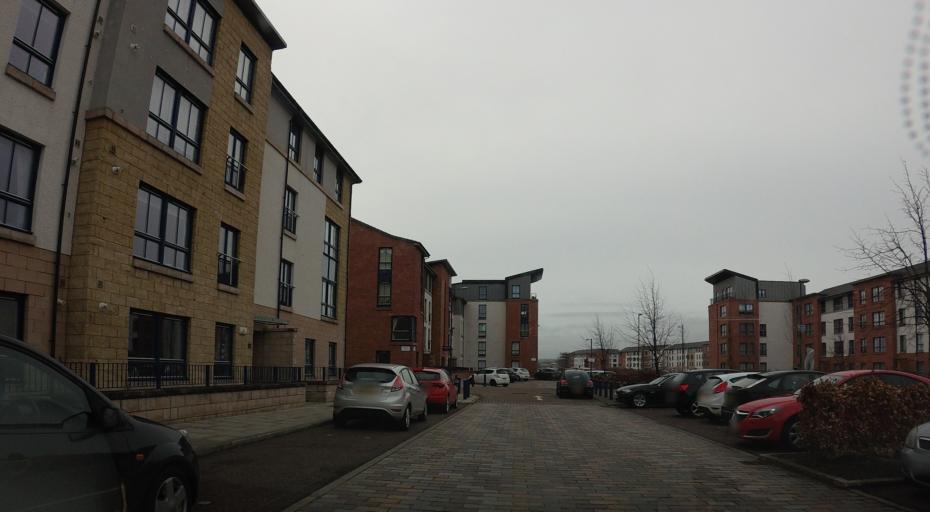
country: GB
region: Scotland
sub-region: South Lanarkshire
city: Rutherglen
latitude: 55.8416
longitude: -4.2385
